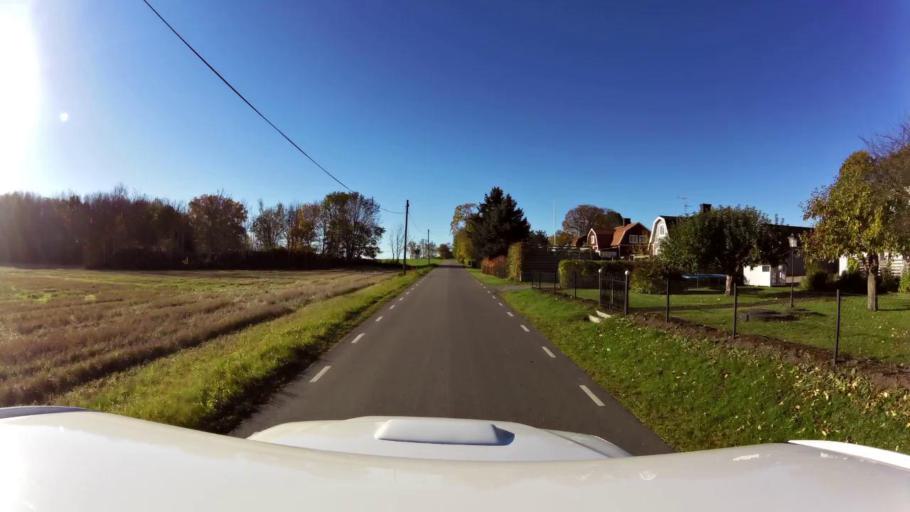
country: SE
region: OEstergoetland
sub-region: Linkopings Kommun
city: Ljungsbro
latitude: 58.5196
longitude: 15.4225
